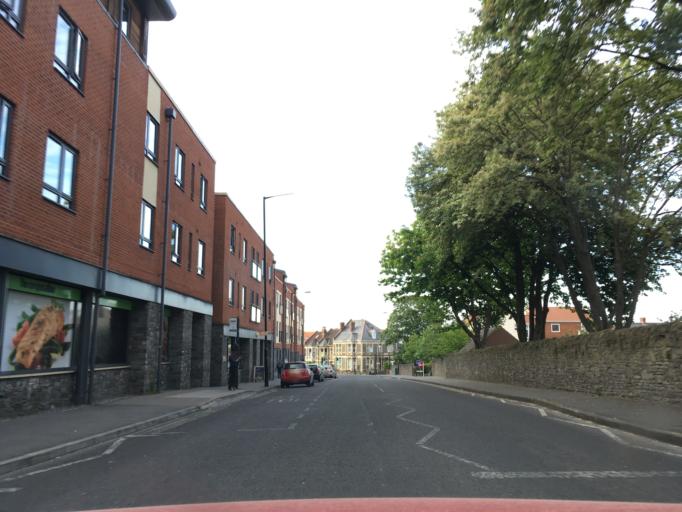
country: GB
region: England
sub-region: Bristol
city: Bristol
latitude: 51.4773
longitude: -2.5799
